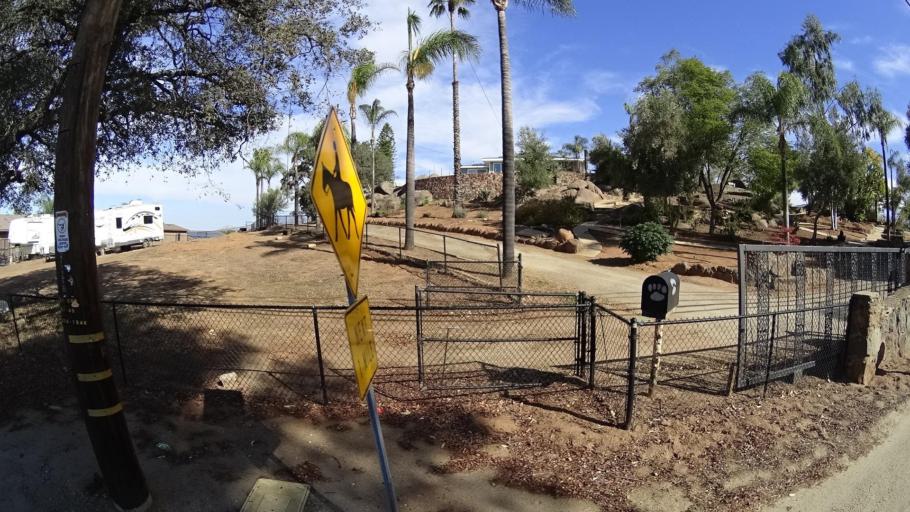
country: US
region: California
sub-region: San Diego County
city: Alpine
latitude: 32.8191
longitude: -116.7859
